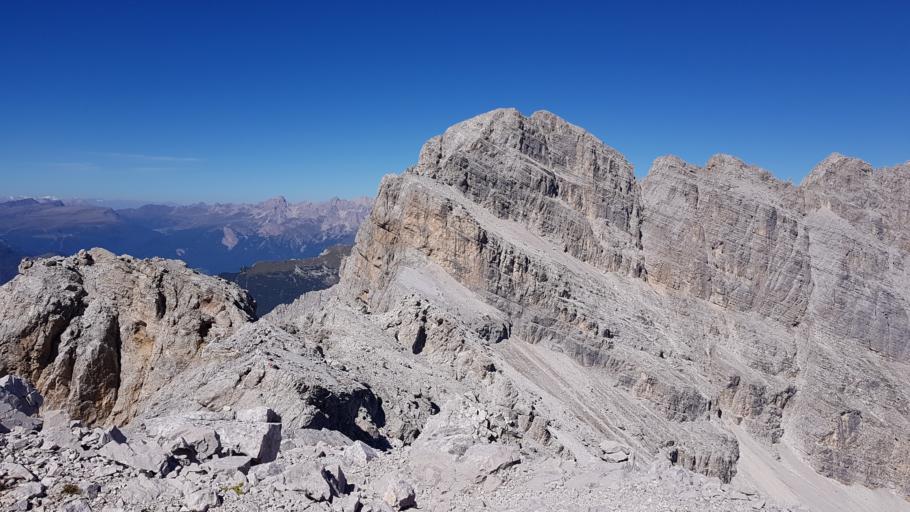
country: IT
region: Veneto
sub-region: Provincia di Belluno
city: La Valle Agordina
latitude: 46.3321
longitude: 12.0676
